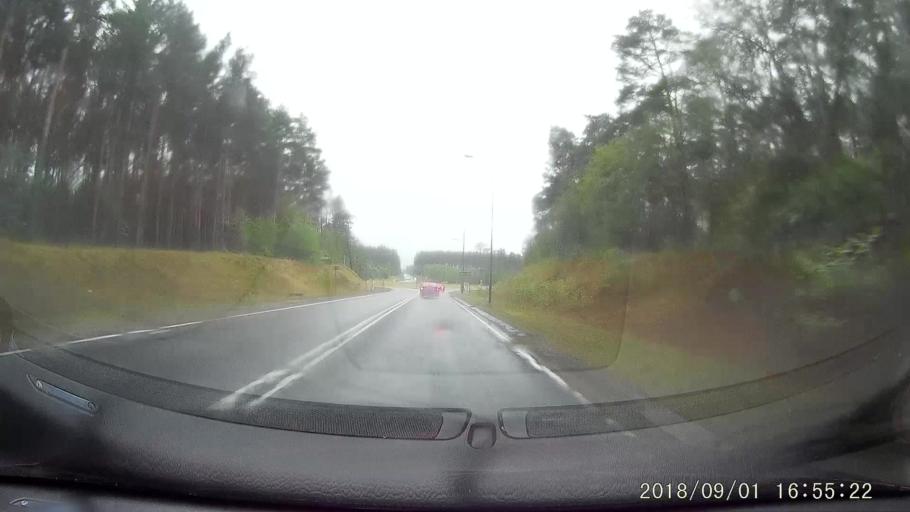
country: PL
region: Lubusz
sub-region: Zielona Gora
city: Zielona Gora
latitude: 51.9486
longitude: 15.4411
